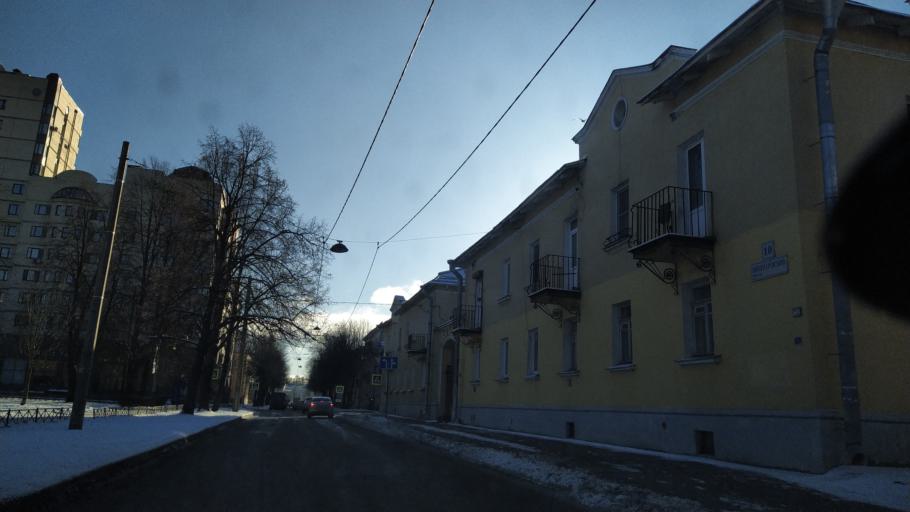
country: RU
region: St.-Petersburg
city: Novaya Derevnya
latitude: 59.9858
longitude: 30.2846
